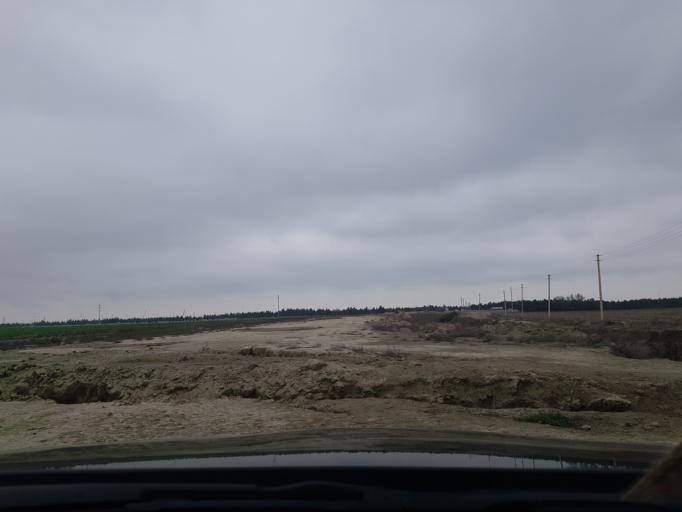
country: TM
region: Ahal
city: Abadan
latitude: 38.1443
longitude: 57.9810
